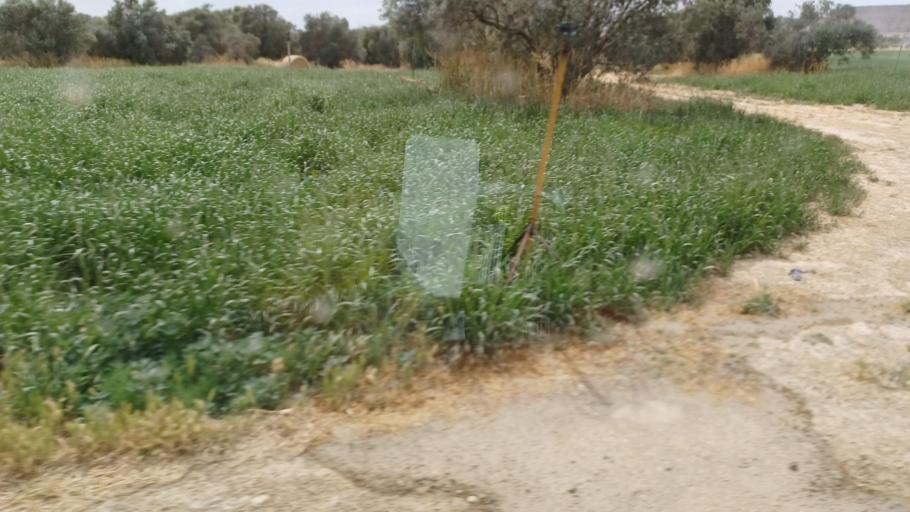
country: CY
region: Larnaka
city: Athienou
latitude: 35.0741
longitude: 33.5392
